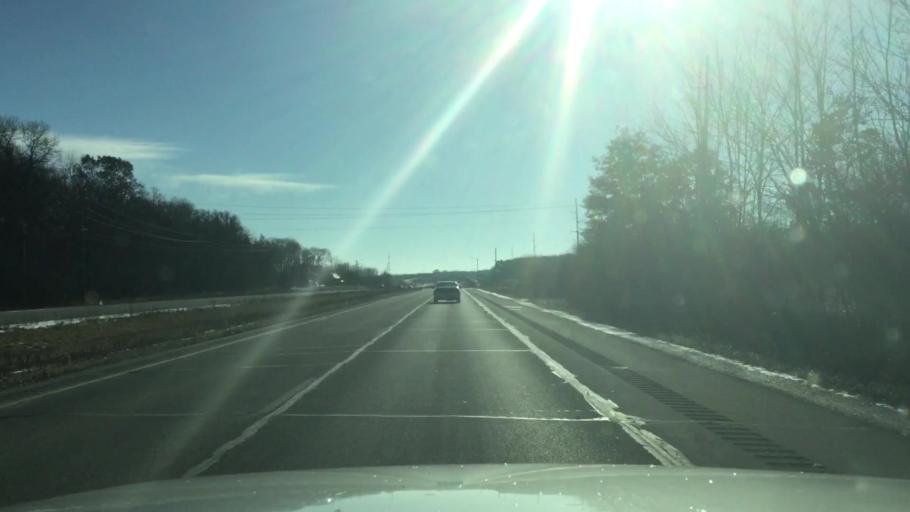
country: US
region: Wisconsin
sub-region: Racine County
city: Rochester
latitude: 42.7292
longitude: -88.2209
